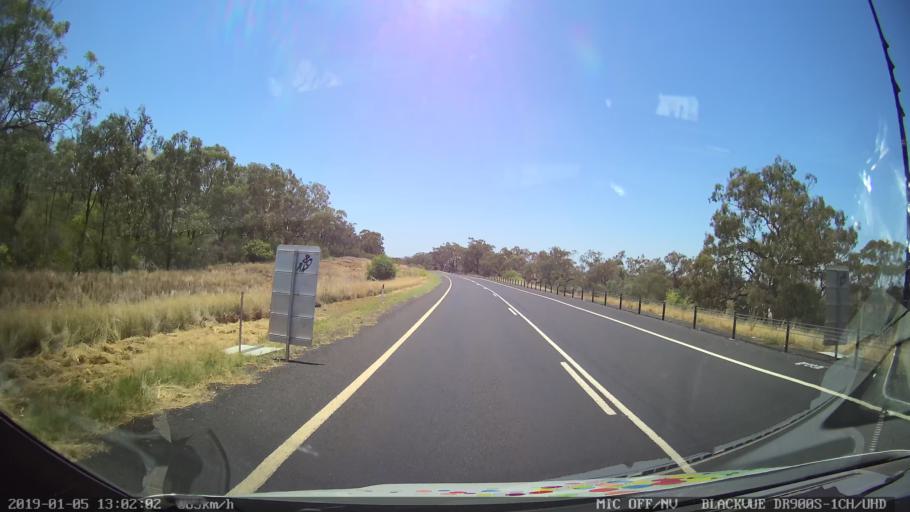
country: AU
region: New South Wales
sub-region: Narrabri
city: Boggabri
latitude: -31.1165
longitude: 149.8057
